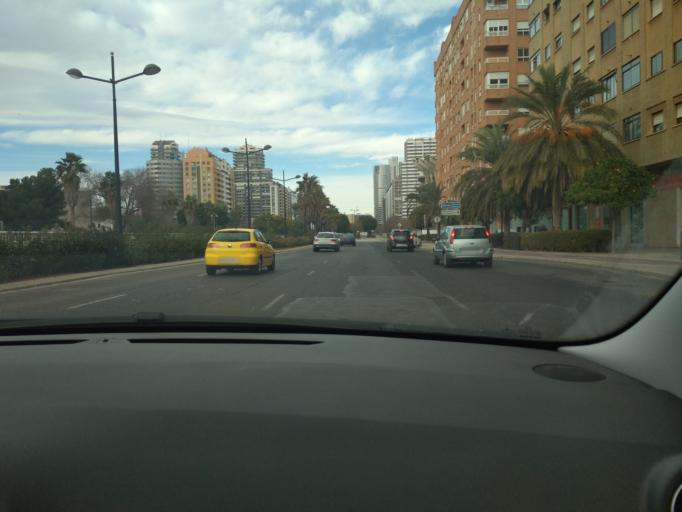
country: ES
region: Valencia
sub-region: Provincia de Valencia
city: Mislata
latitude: 39.4866
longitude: -0.3964
